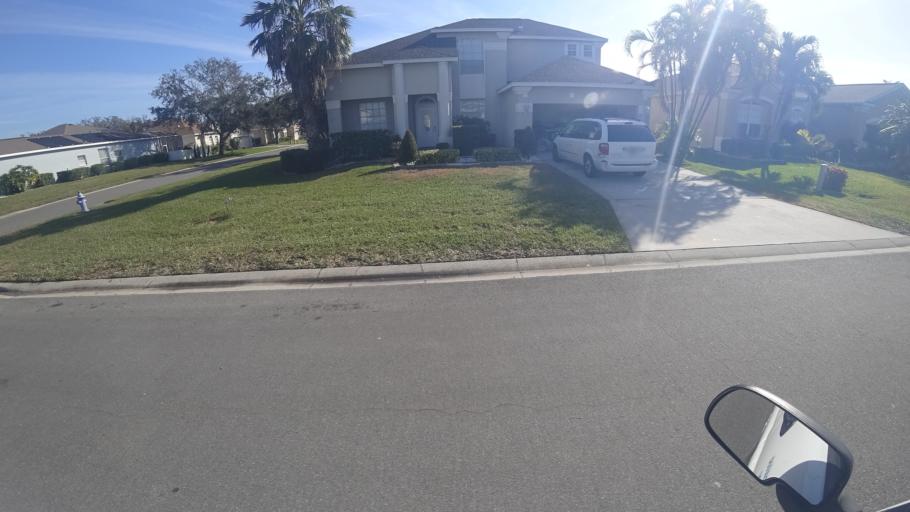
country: US
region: Florida
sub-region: Manatee County
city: South Bradenton
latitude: 27.4513
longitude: -82.6153
